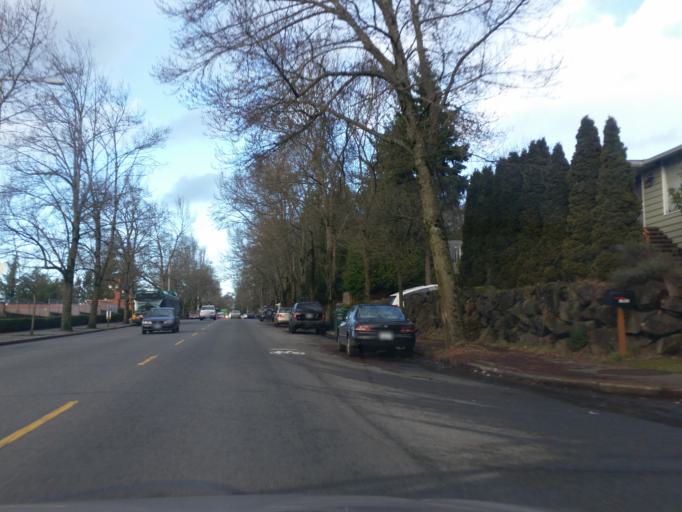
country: US
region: Washington
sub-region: King County
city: Lake Forest Park
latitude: 47.7230
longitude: -122.2908
